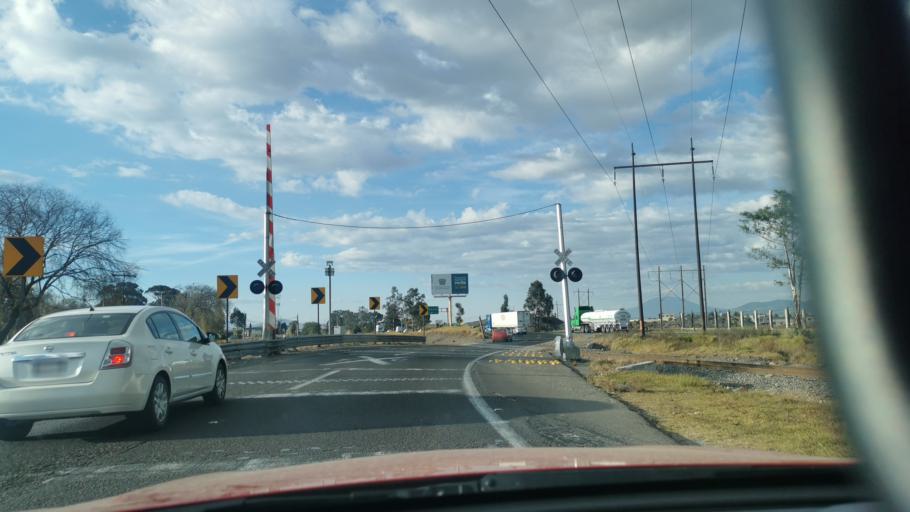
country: MX
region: Mexico
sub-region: Toluca
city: Colonia Aviacion Autopan
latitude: 19.3806
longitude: -99.7039
